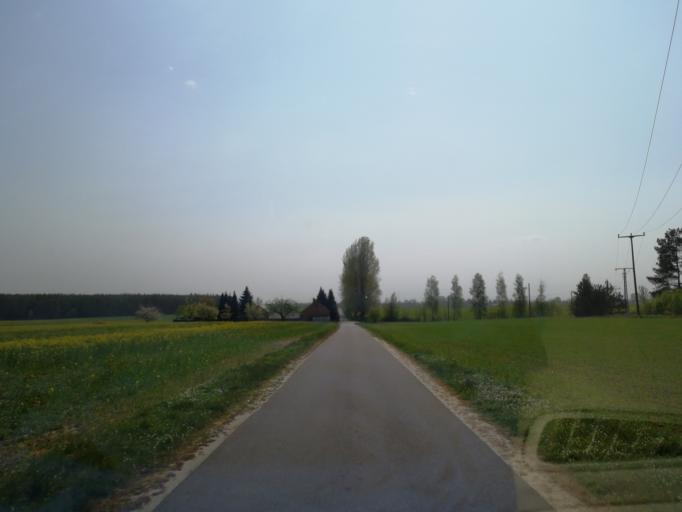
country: DE
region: Brandenburg
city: Bronkow
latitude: 51.6507
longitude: 13.8567
